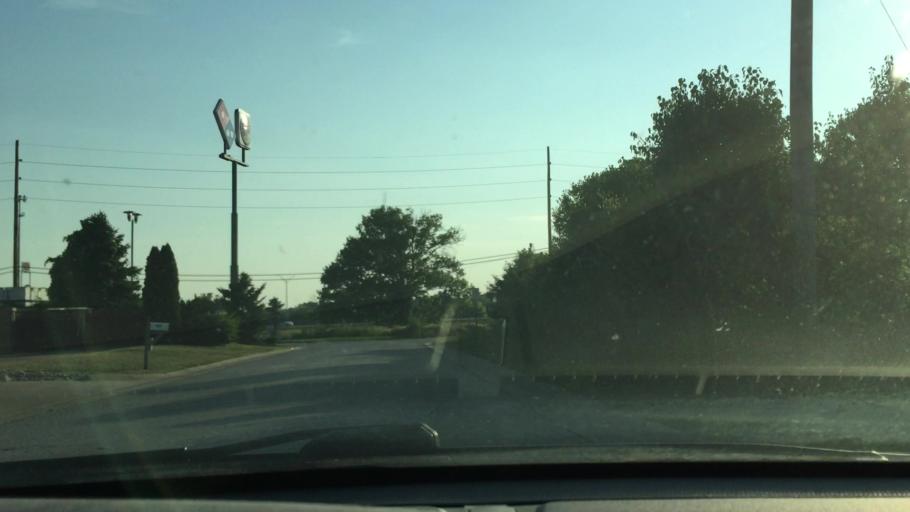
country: US
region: Kentucky
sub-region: Boone County
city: Walton
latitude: 38.9190
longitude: -84.6268
